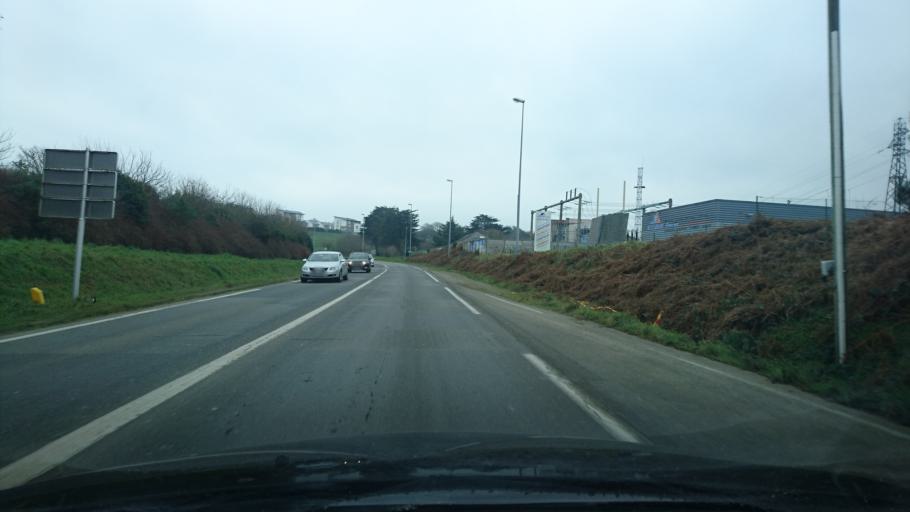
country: FR
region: Brittany
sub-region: Departement du Finistere
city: Guilers
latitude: 48.3925
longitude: -4.5393
